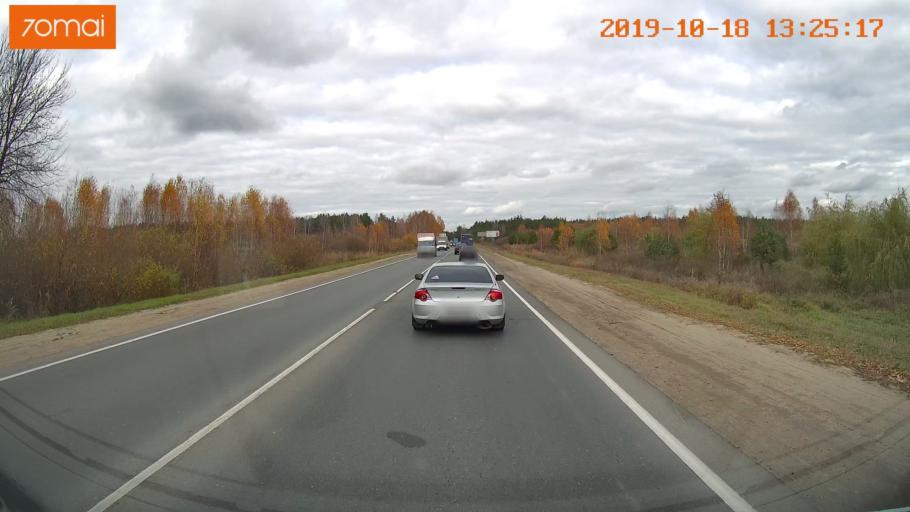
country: RU
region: Rjazan
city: Polyany
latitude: 54.7415
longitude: 39.8409
